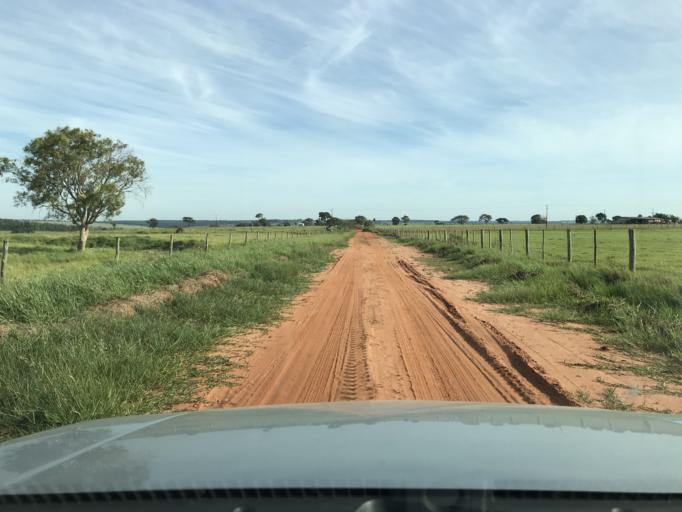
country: BR
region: Mato Grosso do Sul
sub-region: Iguatemi
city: Iguatemi
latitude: -23.6576
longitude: -54.5700
